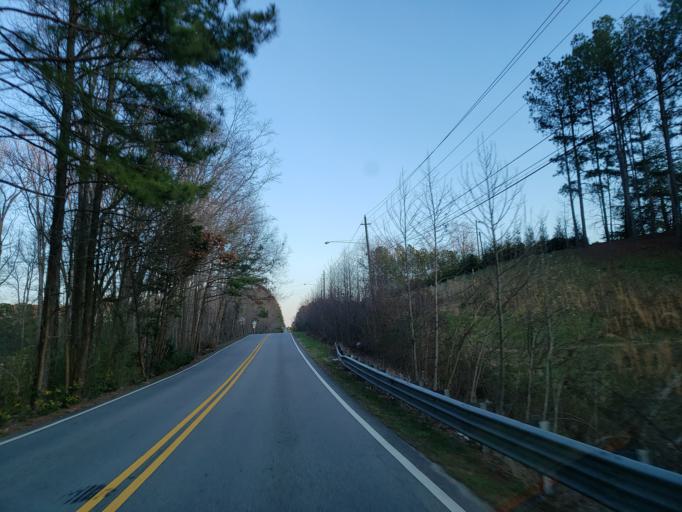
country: US
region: Georgia
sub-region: Cobb County
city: Acworth
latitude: 33.9943
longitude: -84.7226
